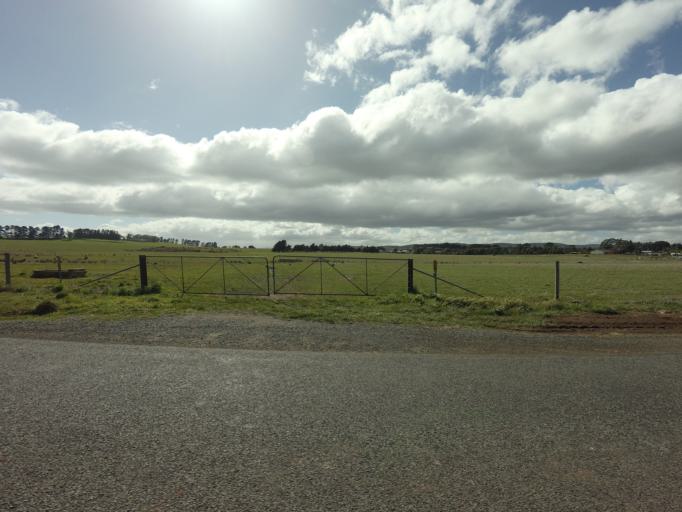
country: AU
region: Tasmania
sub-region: Northern Midlands
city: Evandale
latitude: -41.9200
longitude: 147.4800
